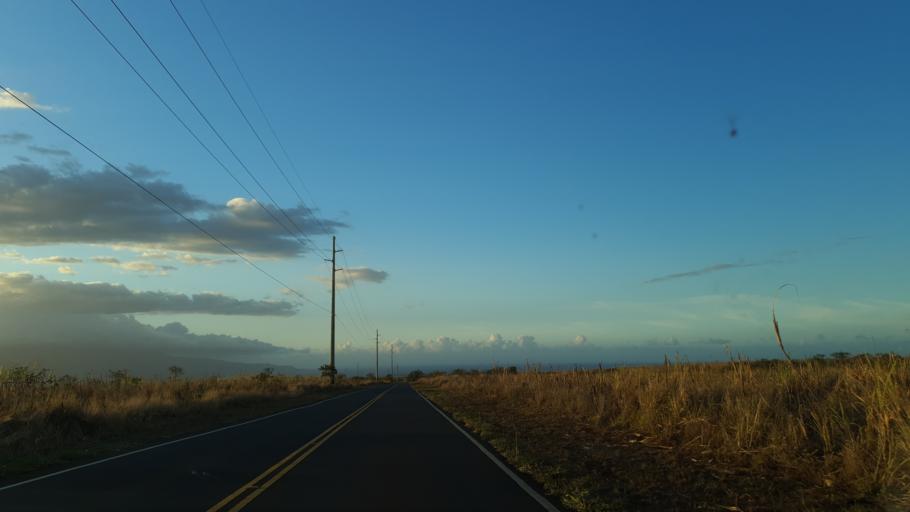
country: US
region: Hawaii
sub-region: Maui County
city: Pukalani
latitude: 20.8090
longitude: -156.3811
